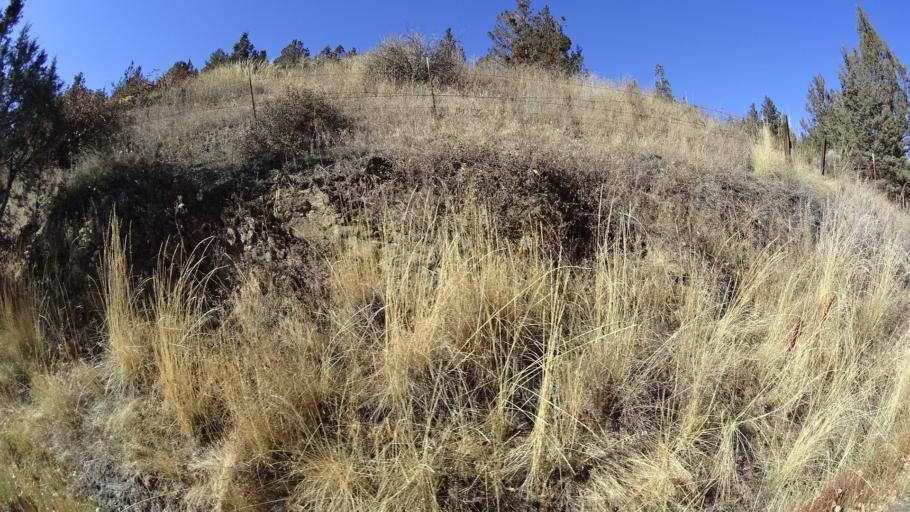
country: US
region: California
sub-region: Siskiyou County
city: Weed
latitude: 41.4816
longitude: -122.5724
